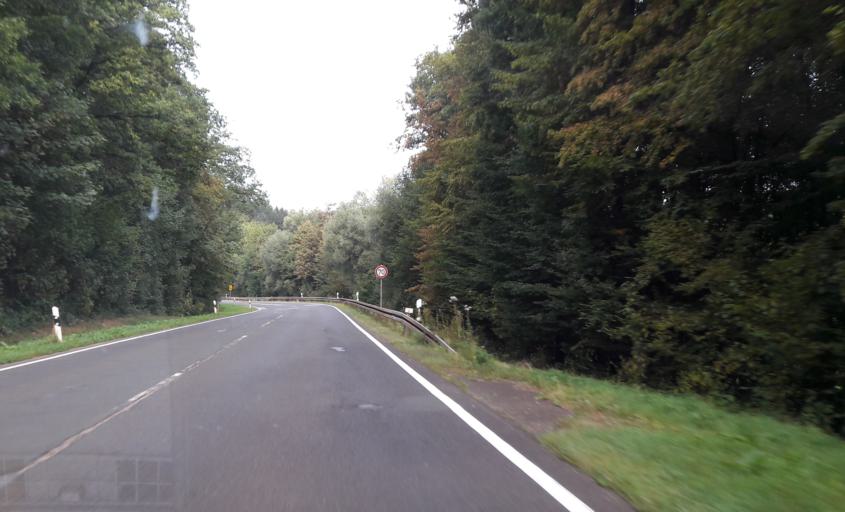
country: DE
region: Rheinland-Pfalz
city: Ellweiler
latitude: 49.6104
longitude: 7.1698
